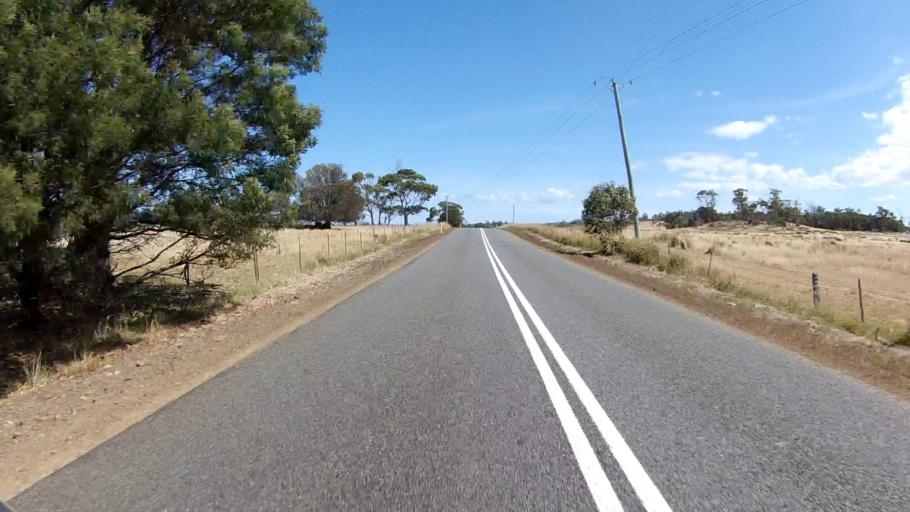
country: AU
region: Tasmania
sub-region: Sorell
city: Sorell
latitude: -42.2891
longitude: 147.9943
